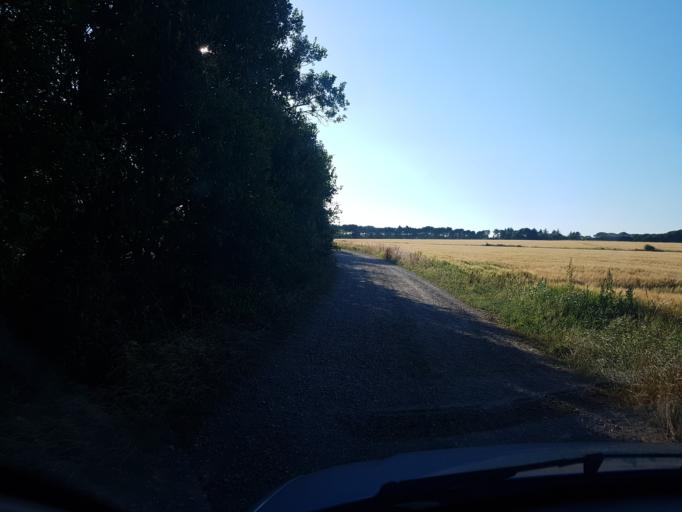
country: DK
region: South Denmark
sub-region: Esbjerg Kommune
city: Tjaereborg
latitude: 55.4930
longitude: 8.5201
